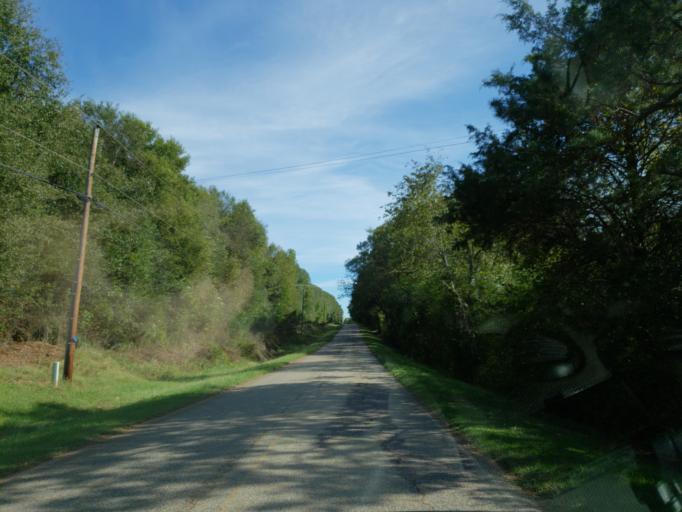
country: US
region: Georgia
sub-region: Crawford County
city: Roberta
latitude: 32.8579
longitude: -84.0861
